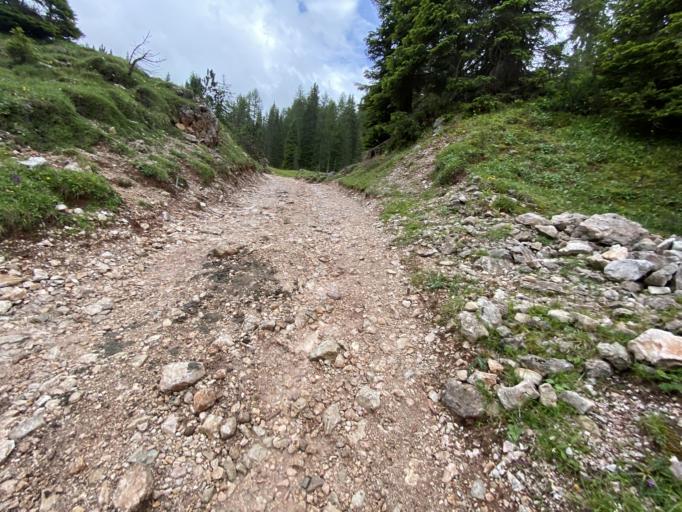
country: IT
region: Veneto
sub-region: Provincia di Belluno
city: Cortina d'Ampezzo
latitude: 46.4858
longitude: 12.1154
